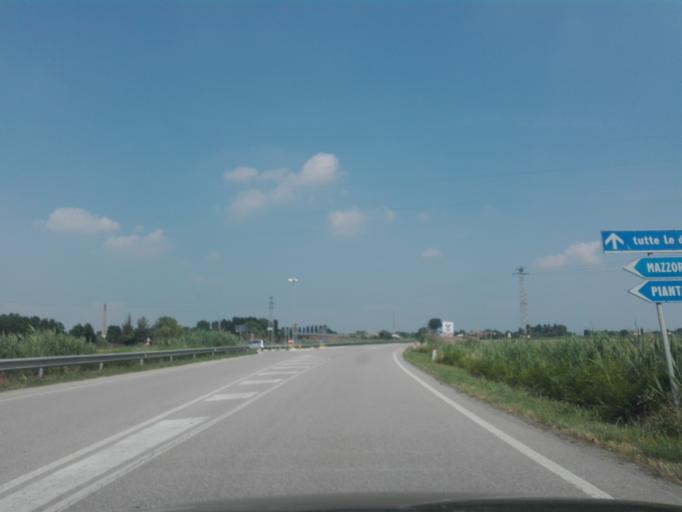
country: IT
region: Veneto
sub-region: Provincia di Rovigo
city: Adria
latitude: 45.0466
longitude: 12.0674
